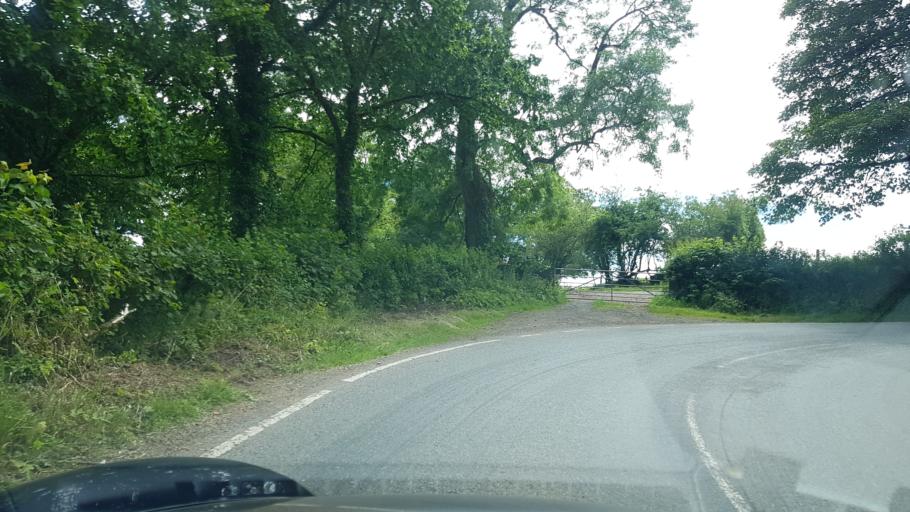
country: GB
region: Wales
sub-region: Carmarthenshire
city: Llanddowror
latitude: 51.7655
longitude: -4.5690
